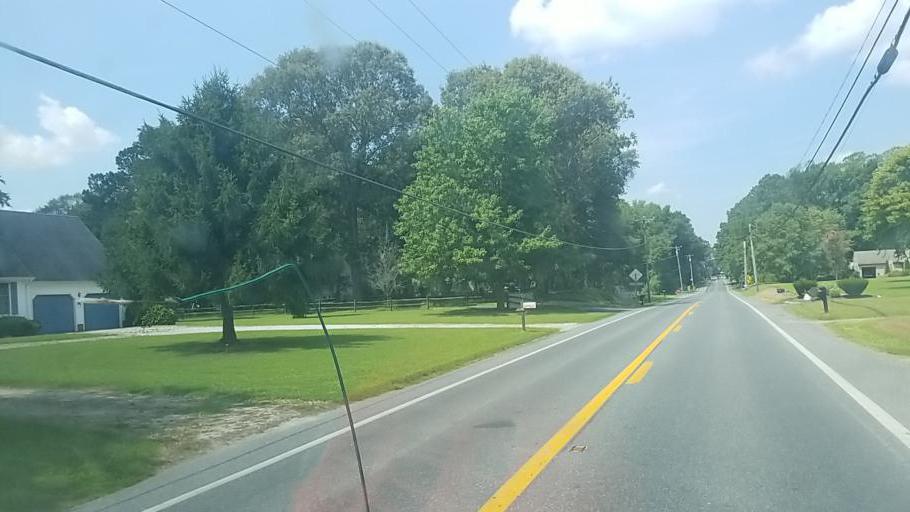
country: US
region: Maryland
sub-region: Wicomico County
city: Salisbury
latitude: 38.3547
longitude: -75.5309
